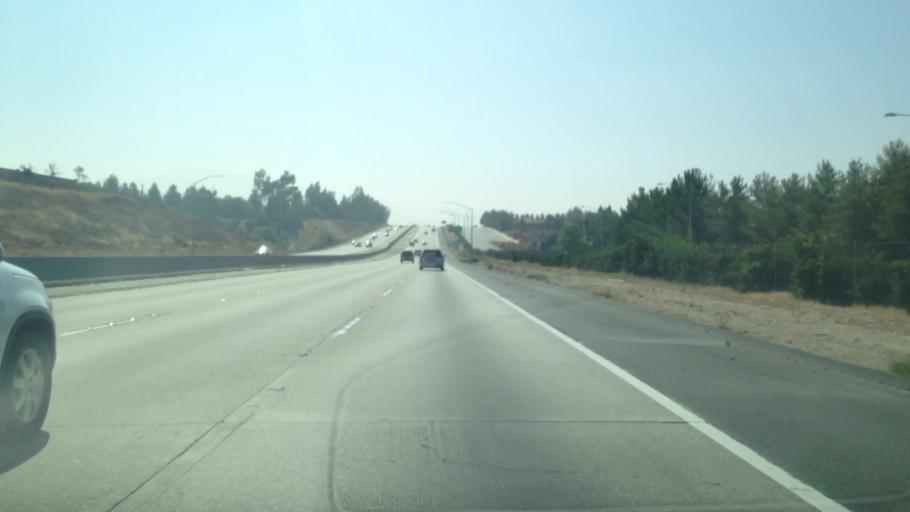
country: US
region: California
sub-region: Riverside County
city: Cherry Valley
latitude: 33.9542
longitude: -117.0152
